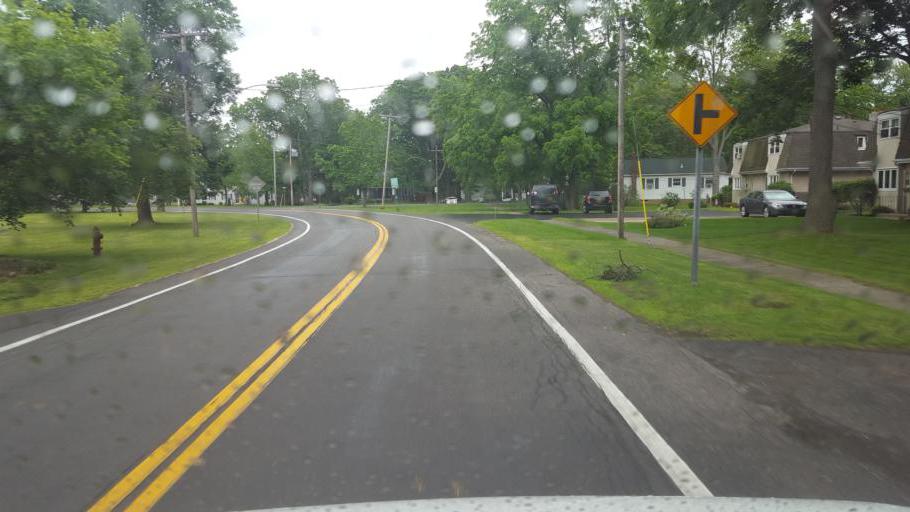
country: US
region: New York
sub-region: Niagara County
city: Youngstown
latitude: 43.2549
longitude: -79.0482
